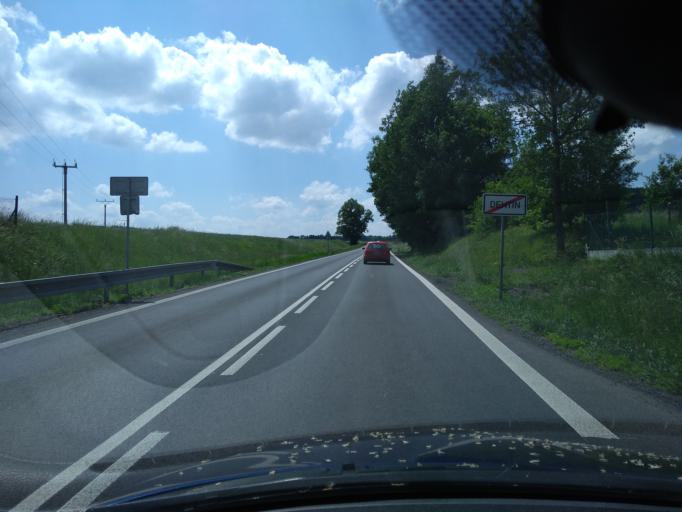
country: CZ
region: Plzensky
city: Svihov
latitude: 49.4470
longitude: 13.2871
